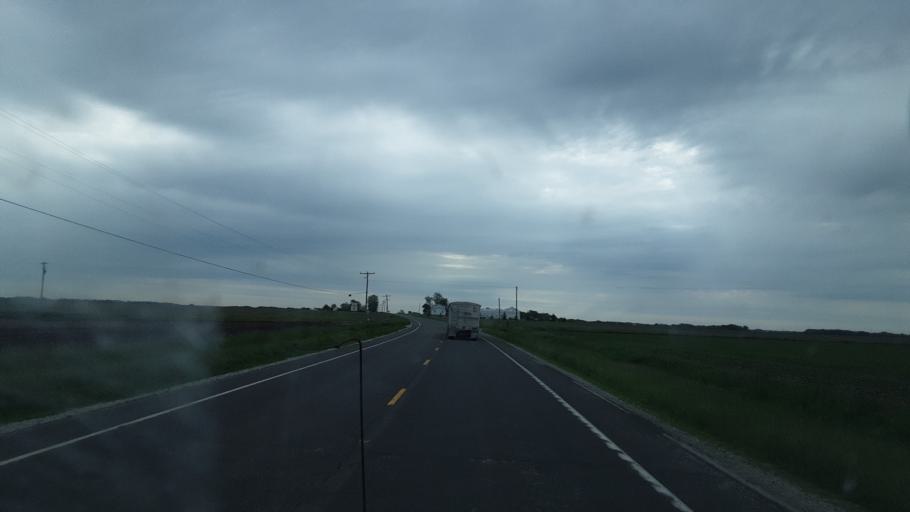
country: US
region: Illinois
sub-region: Fulton County
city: Lewistown
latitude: 40.3414
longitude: -90.2577
